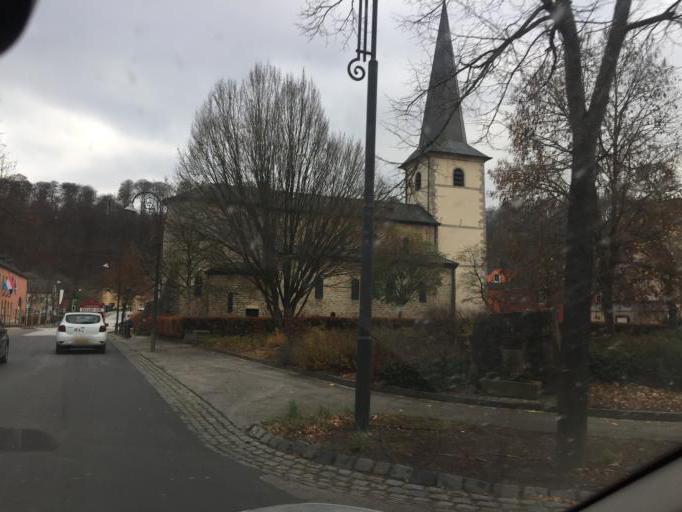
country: LU
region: Diekirch
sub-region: Canton de Redange
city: Saeul
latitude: 49.7275
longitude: 5.9851
